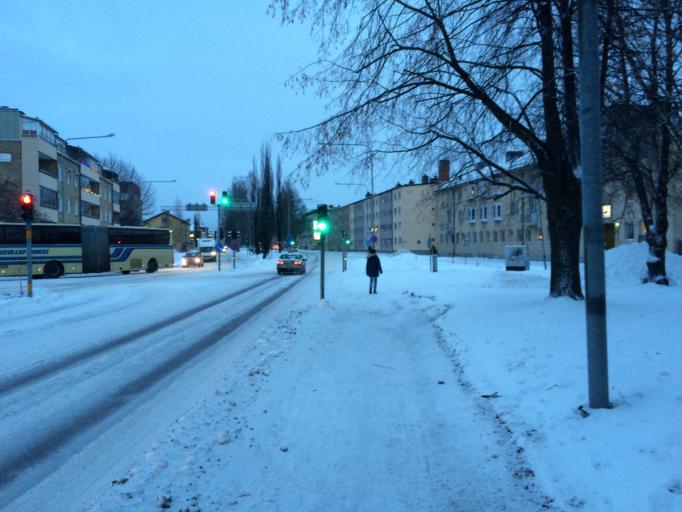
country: SE
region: Vaesterbotten
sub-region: Skelleftea Kommun
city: Skelleftea
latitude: 64.7524
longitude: 20.9448
